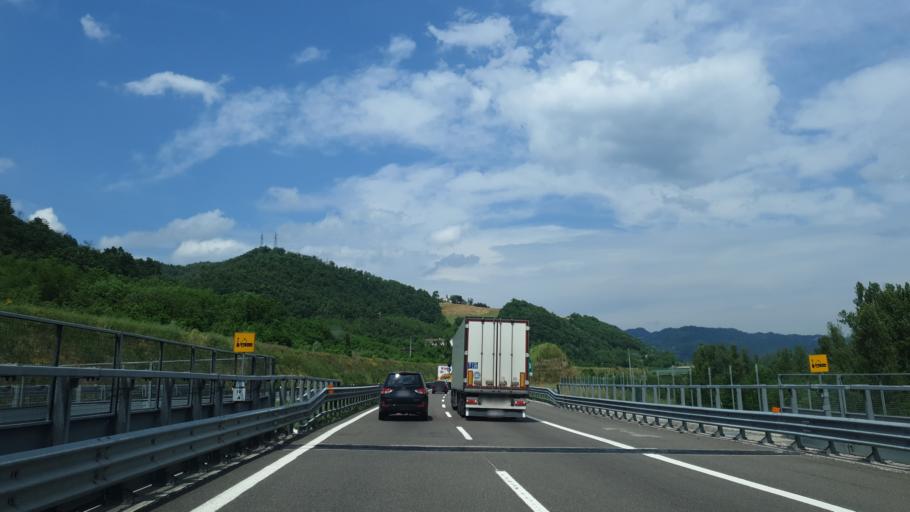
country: IT
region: Emilia-Romagna
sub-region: Provincia di Bologna
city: Grizzana
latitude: 44.2662
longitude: 11.1874
